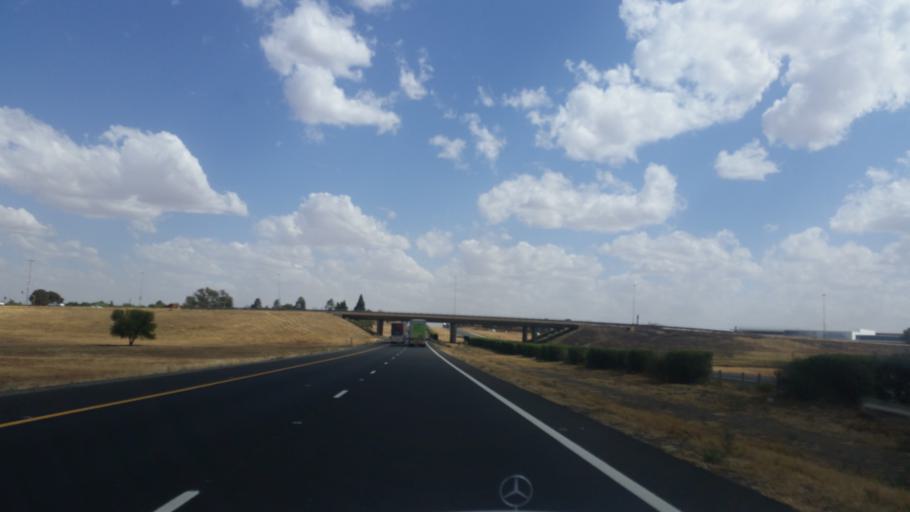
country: ZA
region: Orange Free State
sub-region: Mangaung Metropolitan Municipality
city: Bloemfontein
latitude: -29.0888
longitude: 26.1724
